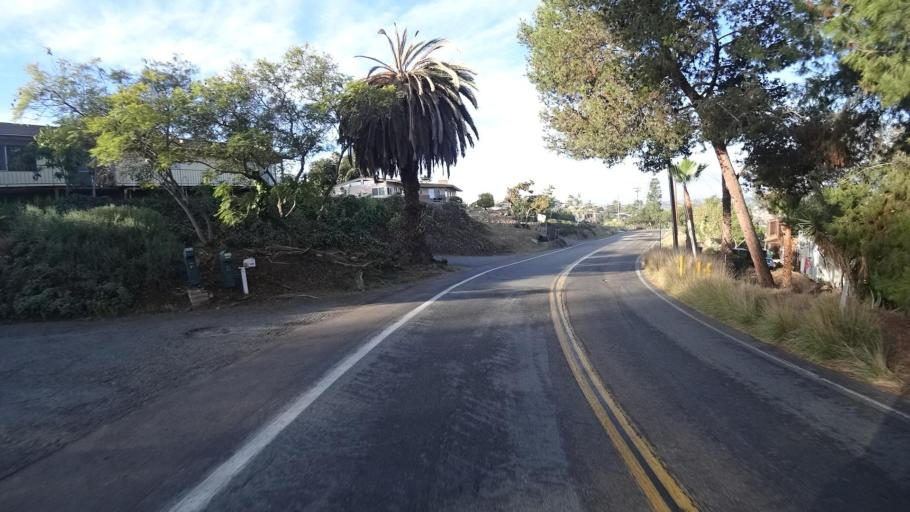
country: US
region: California
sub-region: San Diego County
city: La Presa
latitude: 32.7257
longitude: -117.0018
